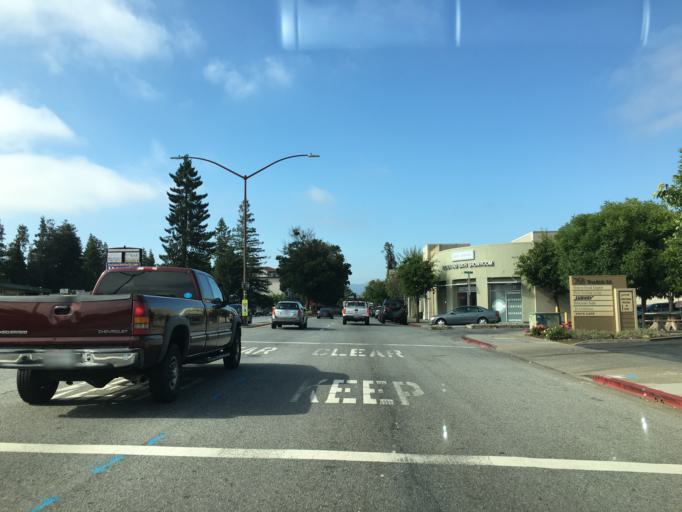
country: US
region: California
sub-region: San Mateo County
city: Redwood City
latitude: 37.4671
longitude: -122.2242
